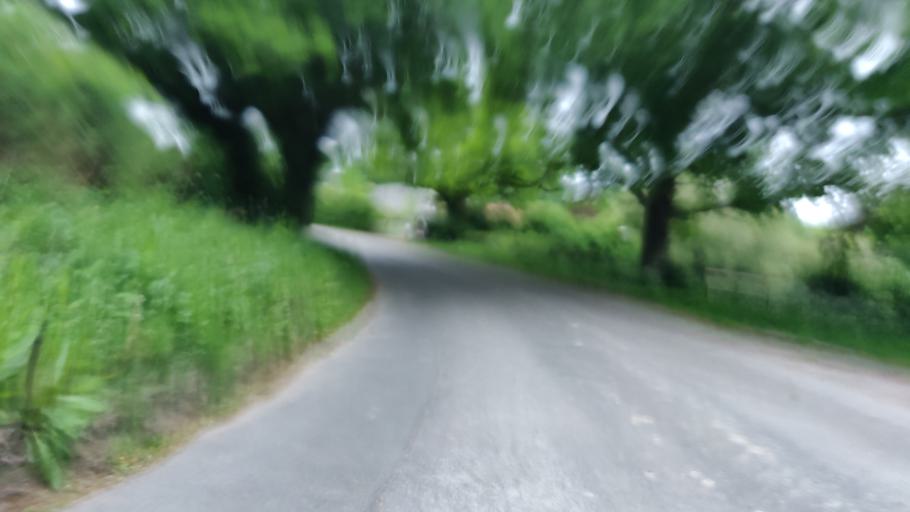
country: GB
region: England
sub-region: West Sussex
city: Partridge Green
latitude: 51.0001
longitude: -0.3036
